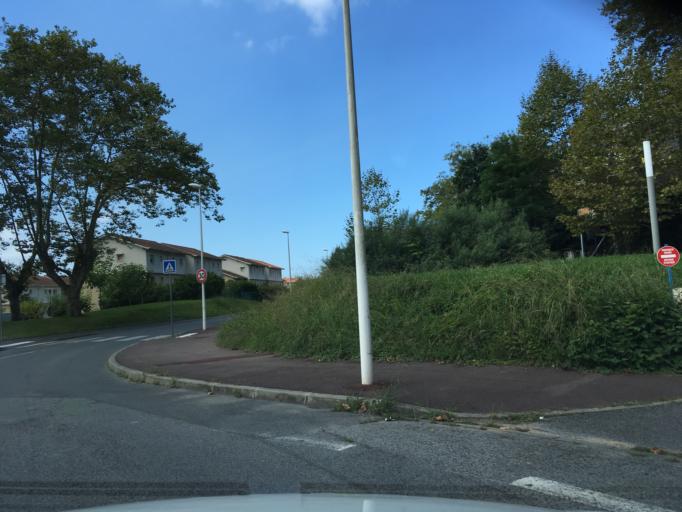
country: FR
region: Aquitaine
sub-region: Departement des Pyrenees-Atlantiques
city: Boucau
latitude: 43.5002
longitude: -1.4504
